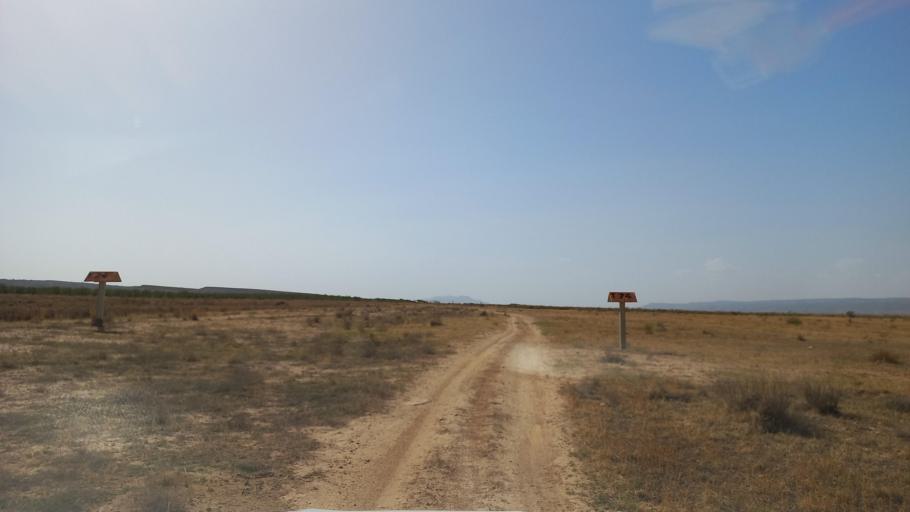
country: TN
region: Al Qasrayn
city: Kasserine
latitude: 35.2140
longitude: 9.0284
